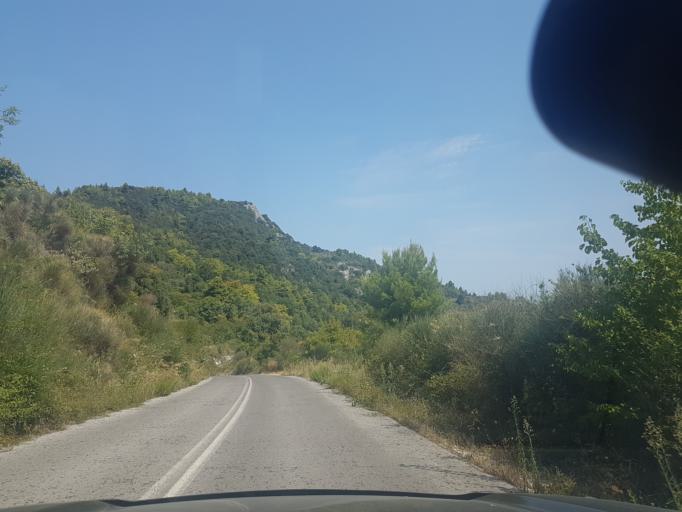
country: GR
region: Central Greece
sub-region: Nomos Evvoias
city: Kymi
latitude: 38.6543
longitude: 23.9136
